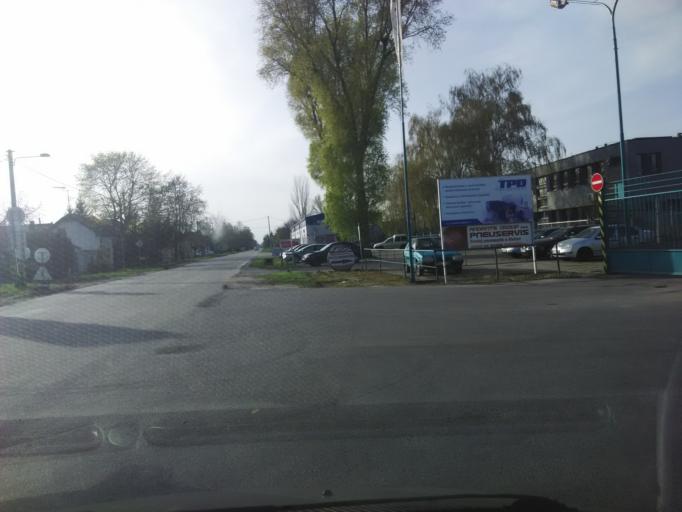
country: SK
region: Nitriansky
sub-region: Okres Nove Zamky
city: Nove Zamky
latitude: 47.9990
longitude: 18.1774
